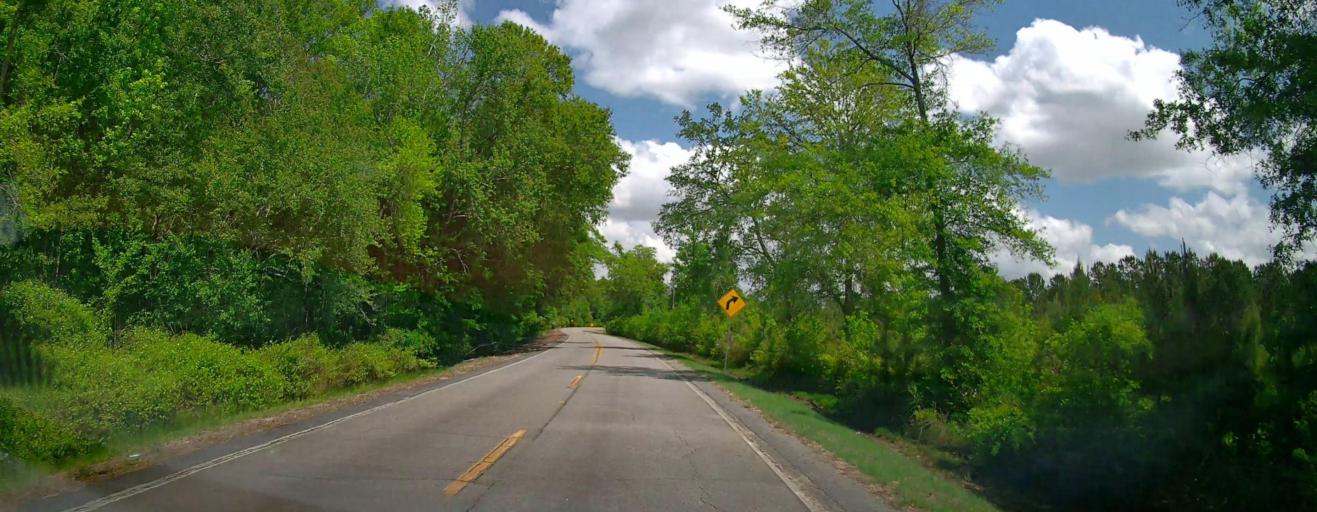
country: US
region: Georgia
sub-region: Bleckley County
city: Cochran
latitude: 32.4618
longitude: -83.2837
